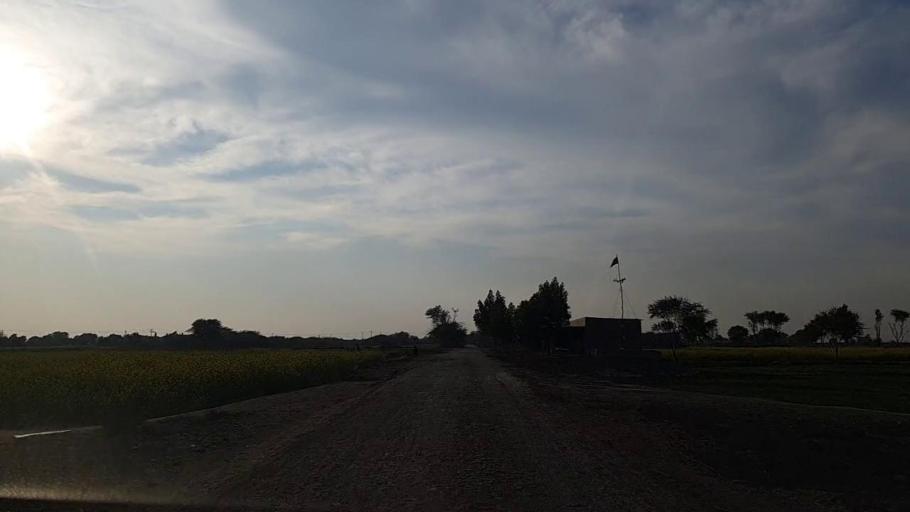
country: PK
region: Sindh
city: Bandhi
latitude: 26.5647
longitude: 68.2621
